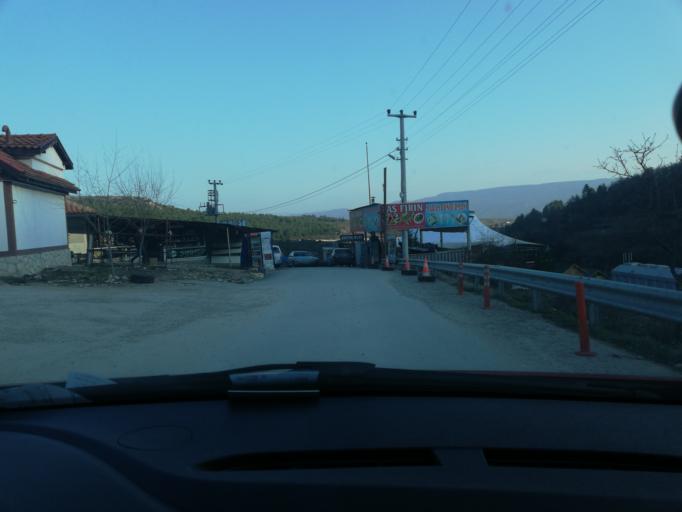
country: TR
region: Karabuk
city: Safranbolu
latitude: 41.2803
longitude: 32.6820
